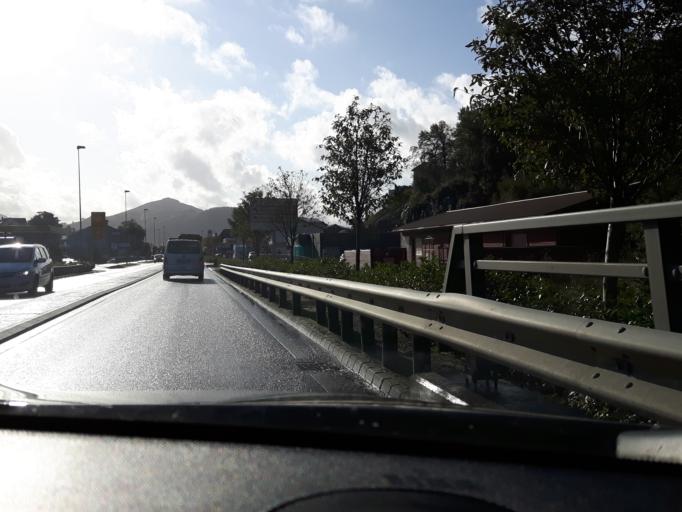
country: NO
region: Rogaland
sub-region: Gjesdal
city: Algard
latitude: 58.7685
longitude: 5.8586
